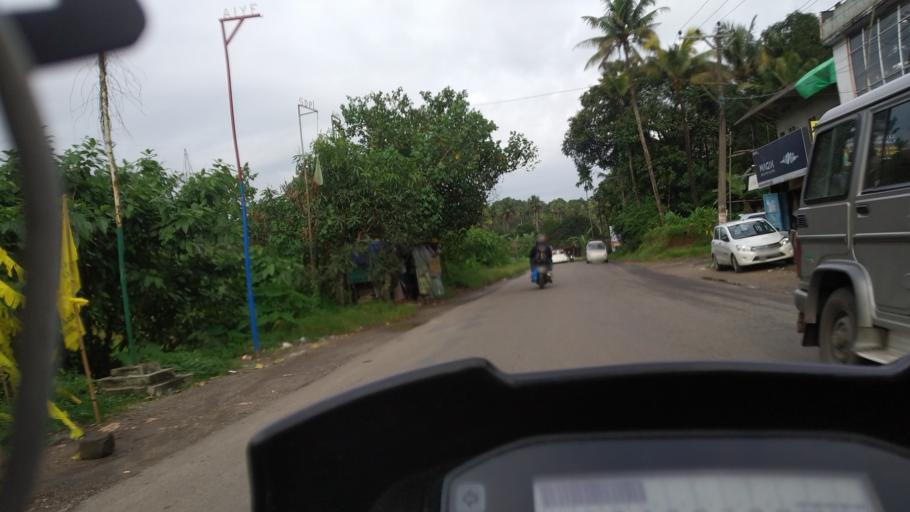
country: IN
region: Kerala
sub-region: Idukki
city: Kuttampuzha
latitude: 10.0506
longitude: 76.7361
